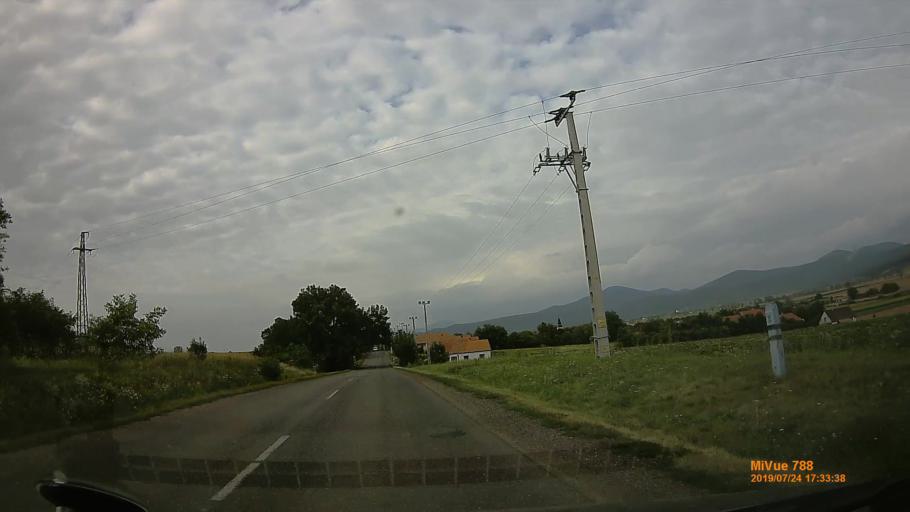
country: HU
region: Borsod-Abauj-Zemplen
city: Abaujszanto
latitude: 48.2963
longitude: 21.1926
